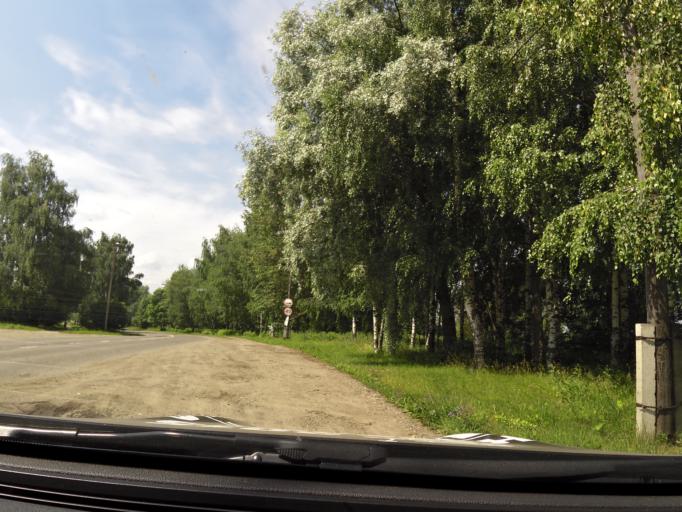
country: RU
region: Kostroma
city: Galich
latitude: 58.3908
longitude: 42.3587
